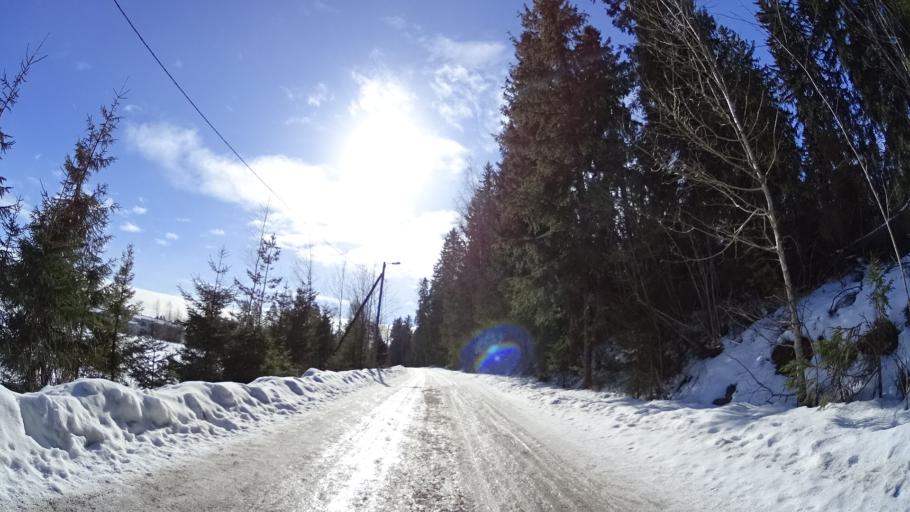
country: FI
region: Uusimaa
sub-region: Helsinki
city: Kauniainen
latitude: 60.2262
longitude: 24.6931
